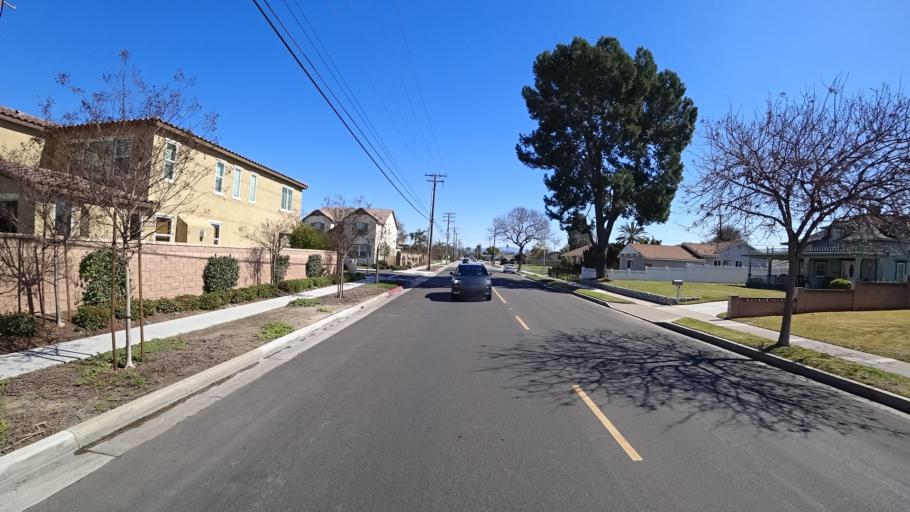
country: US
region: California
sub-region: Orange County
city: Anaheim
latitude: 33.8252
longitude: -117.9471
